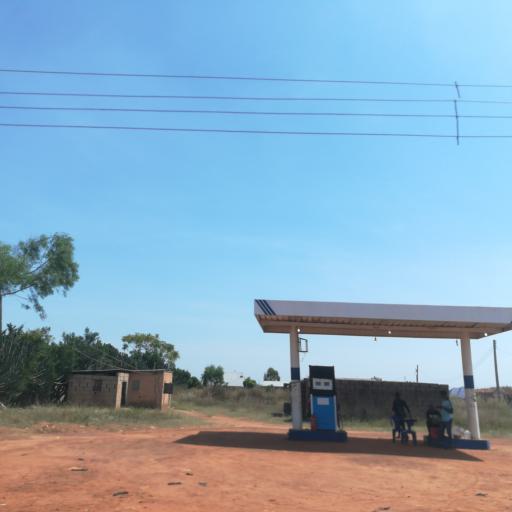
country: NG
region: Plateau
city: Bukuru
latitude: 9.8486
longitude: 8.9249
